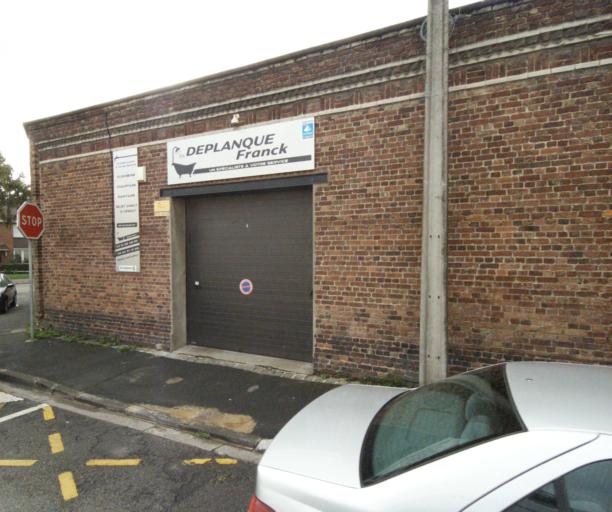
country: FR
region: Nord-Pas-de-Calais
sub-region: Departement du Nord
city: Lambersart
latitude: 50.6476
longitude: 3.0110
